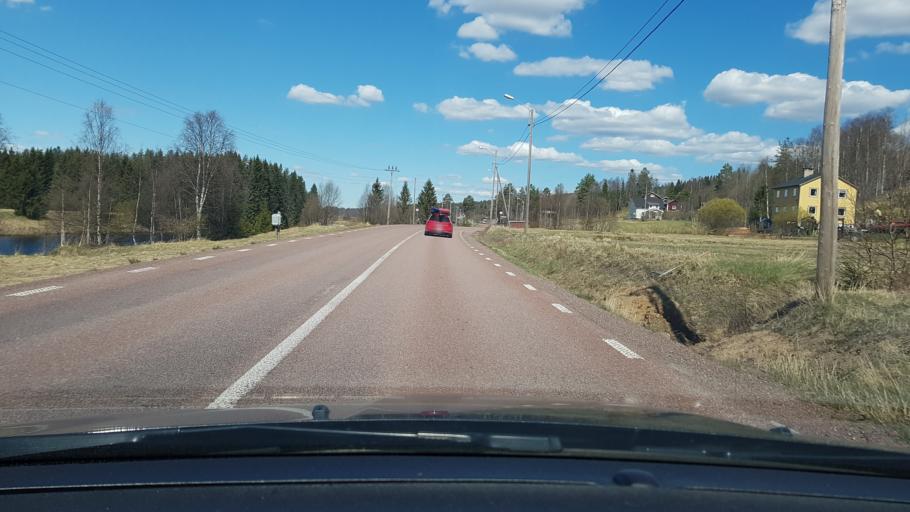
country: SE
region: Dalarna
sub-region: Malung-Saelens kommun
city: Malung
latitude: 61.0836
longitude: 13.3236
